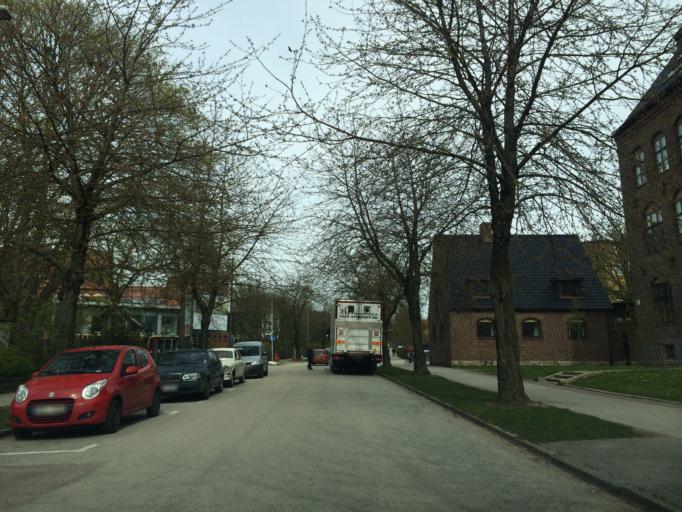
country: SE
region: Skane
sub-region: Lunds Kommun
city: Lund
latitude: 55.7088
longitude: 13.2002
